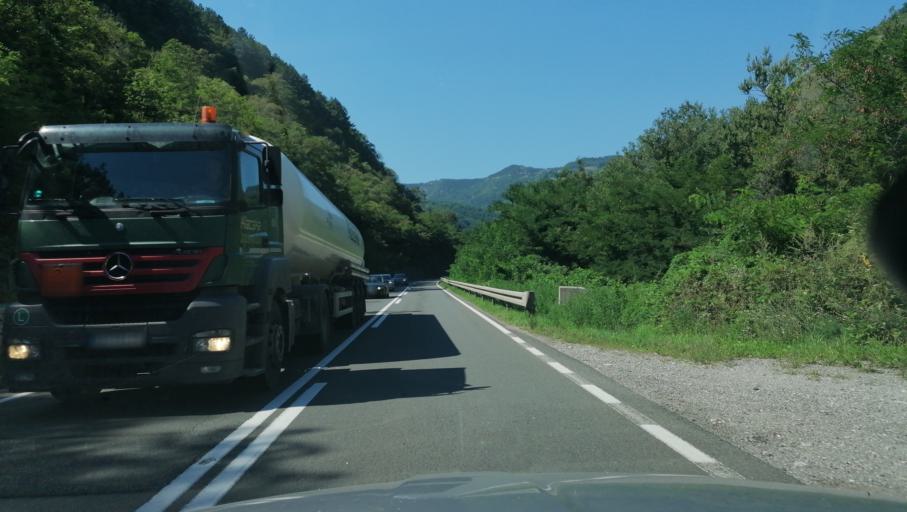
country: RS
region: Central Serbia
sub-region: Raski Okrug
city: Kraljevo
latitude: 43.6200
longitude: 20.5528
